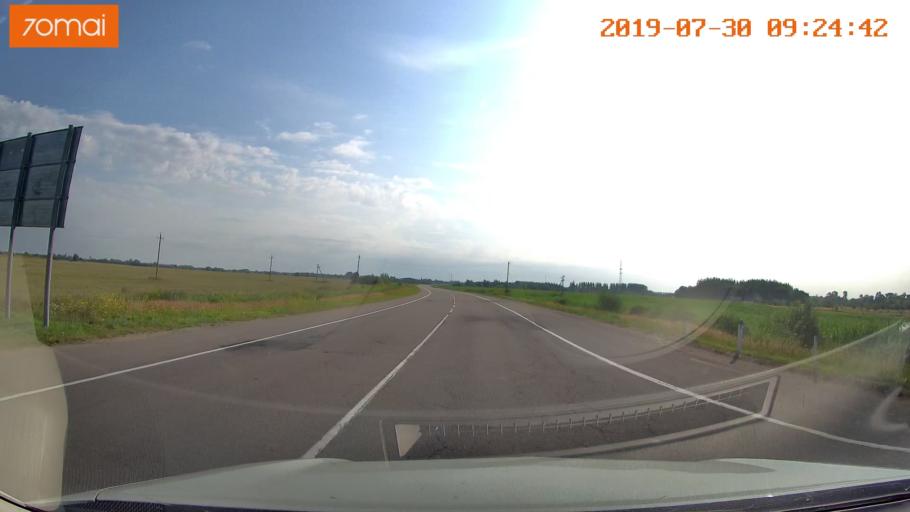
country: LT
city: Kybartai
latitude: 54.6342
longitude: 22.7013
